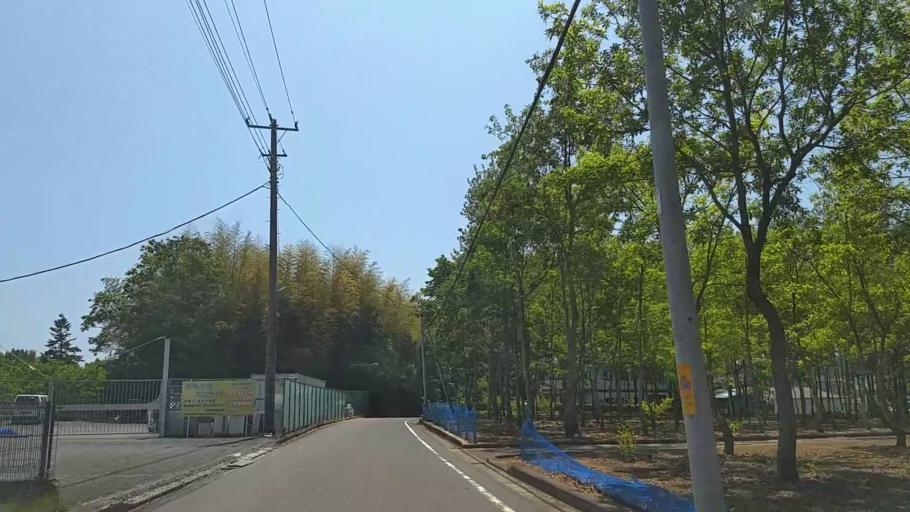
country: JP
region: Shizuoka
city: Mishima
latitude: 35.2041
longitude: 138.9093
